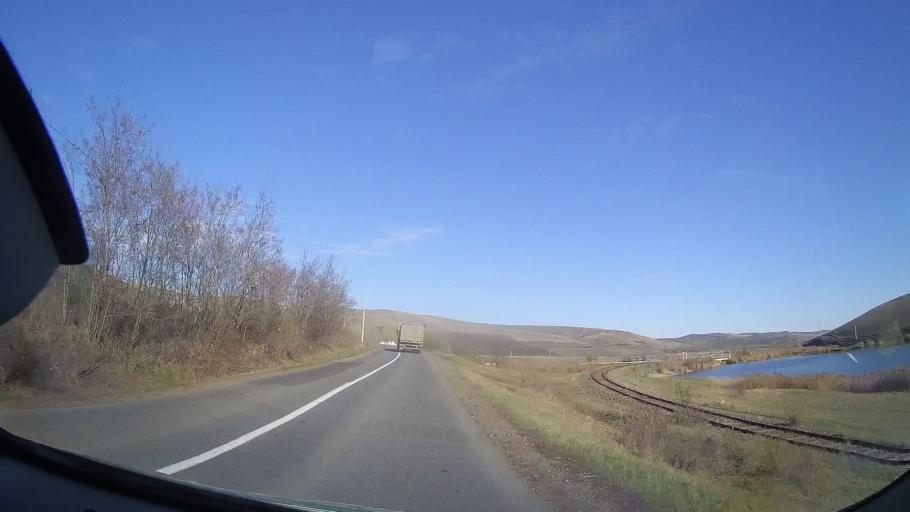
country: RO
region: Mures
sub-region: Comuna Zau De Campie
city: Zau de Campie
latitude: 46.6439
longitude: 24.1460
